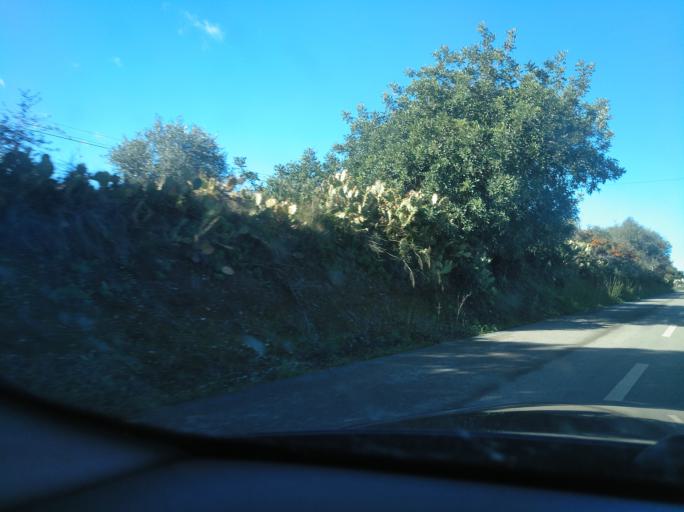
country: PT
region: Faro
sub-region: Vila Real de Santo Antonio
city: Monte Gordo
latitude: 37.1681
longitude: -7.5364
